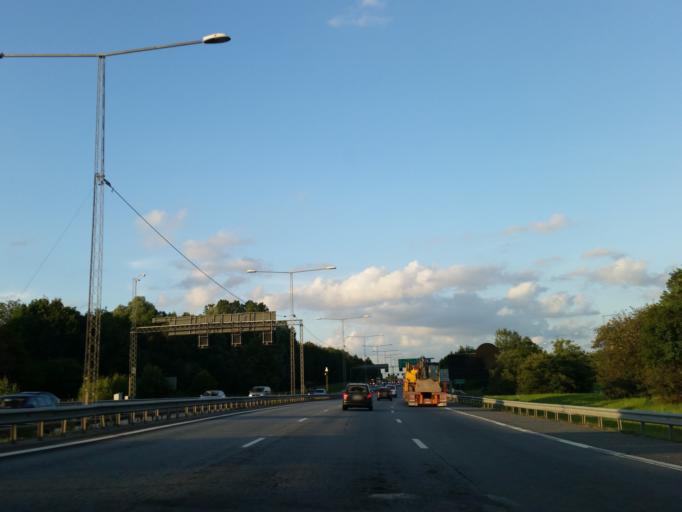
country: SE
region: Stockholm
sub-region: Botkyrka Kommun
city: Fittja
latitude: 59.2470
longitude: 17.8428
